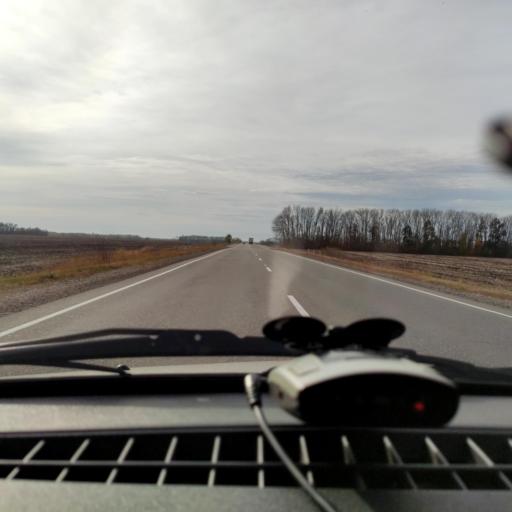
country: RU
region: Voronezj
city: Strelitsa
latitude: 51.5097
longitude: 38.9665
